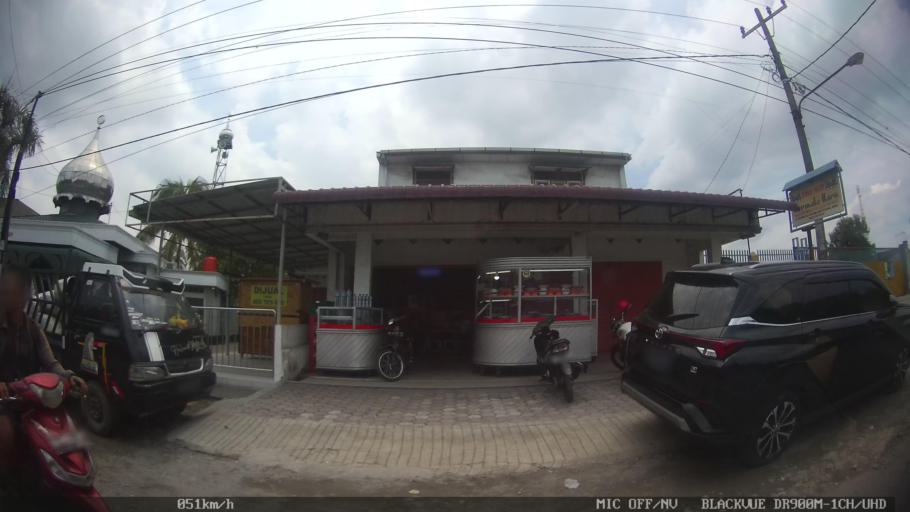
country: ID
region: North Sumatra
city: Labuhan Deli
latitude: 3.6836
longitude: 98.6681
